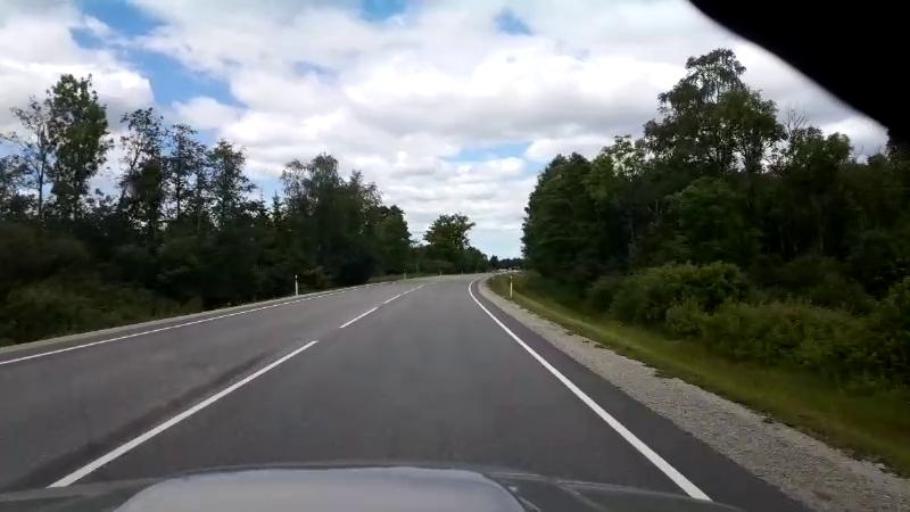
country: EE
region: Raplamaa
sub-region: Maerjamaa vald
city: Marjamaa
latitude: 58.9706
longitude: 24.4759
